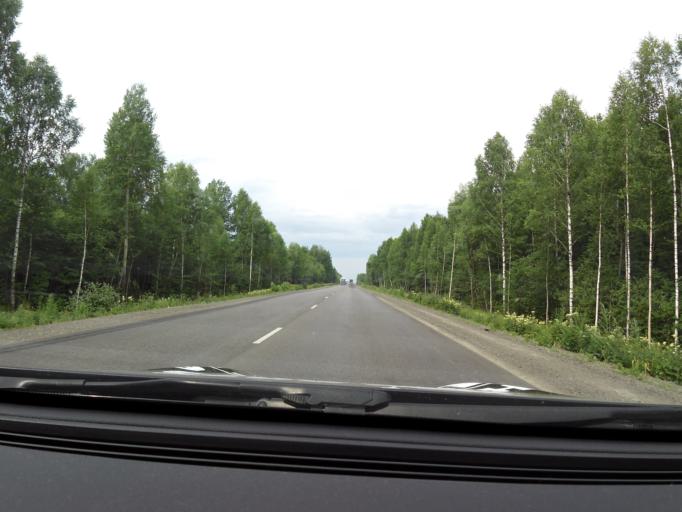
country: RU
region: Chelyabinsk
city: Asha
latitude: 54.8791
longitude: 57.2281
